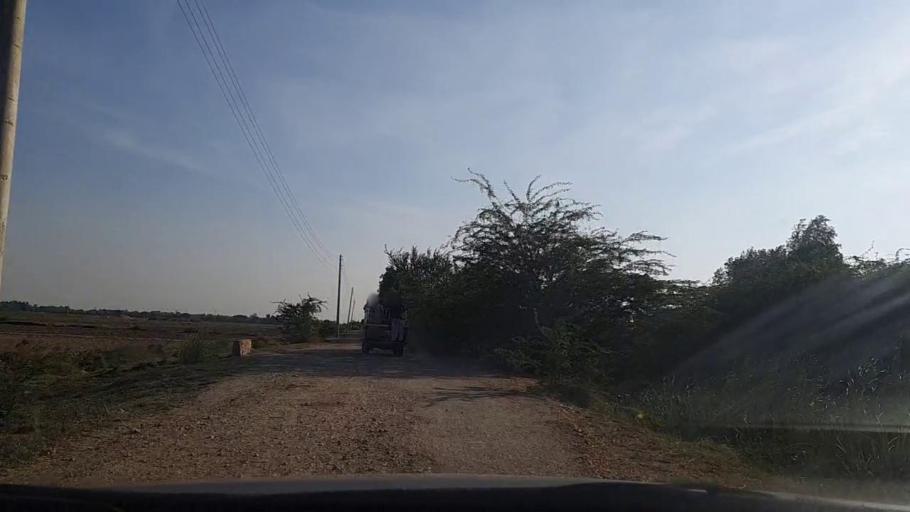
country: PK
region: Sindh
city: Mirpur Sakro
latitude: 24.5320
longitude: 67.6329
